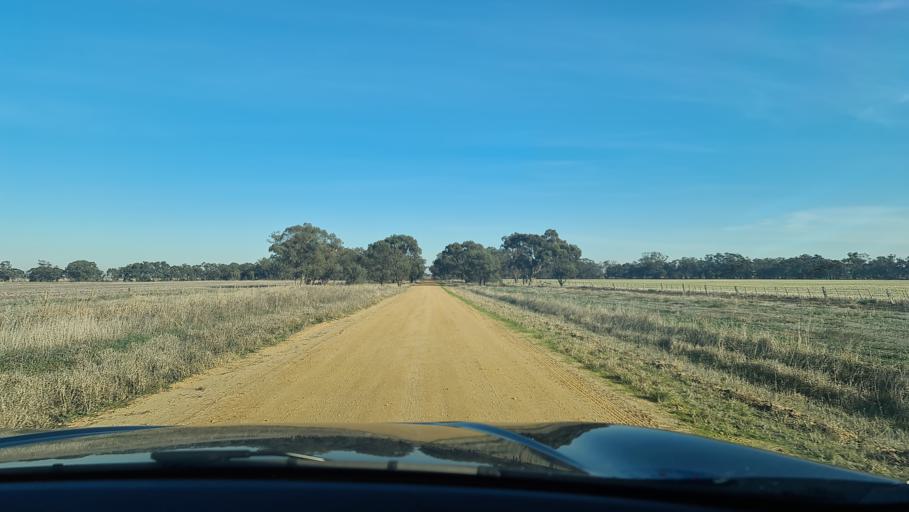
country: AU
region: Victoria
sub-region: Horsham
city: Horsham
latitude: -36.3538
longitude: 142.4021
